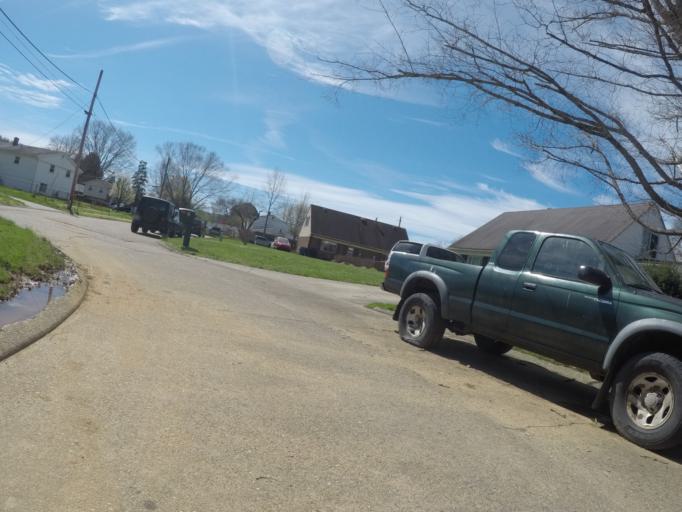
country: US
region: West Virginia
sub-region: Cabell County
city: Pea Ridge
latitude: 38.4040
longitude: -82.3160
